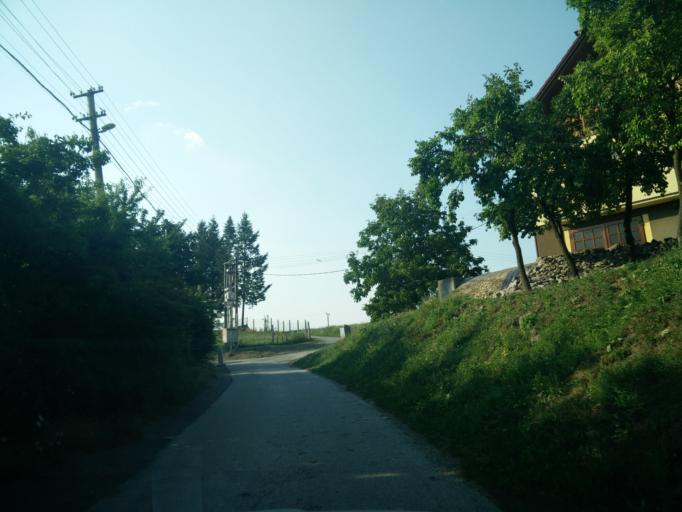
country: SK
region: Nitriansky
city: Prievidza
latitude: 48.7567
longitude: 18.6691
